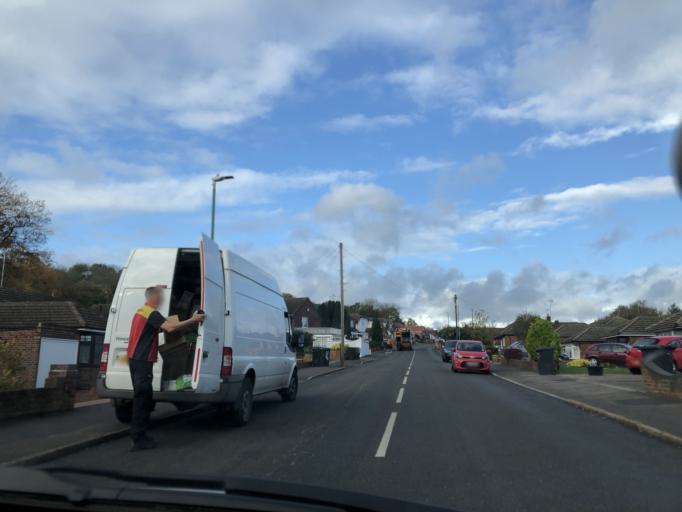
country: GB
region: England
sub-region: Kent
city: Swanley
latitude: 51.4210
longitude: 0.1690
